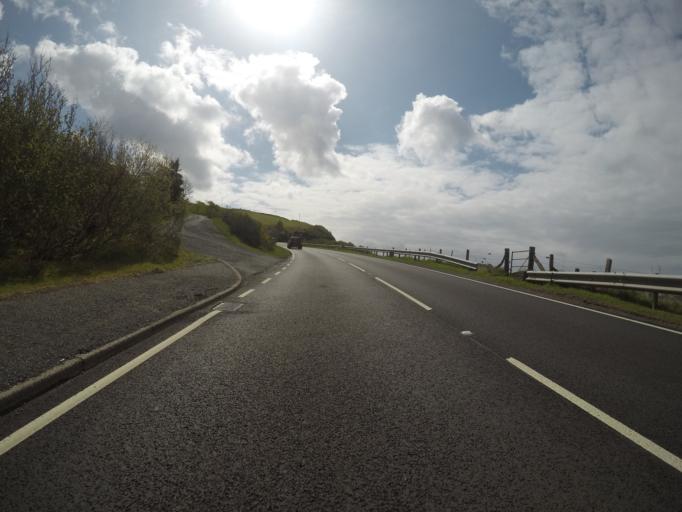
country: GB
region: Scotland
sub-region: Highland
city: Portree
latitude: 57.5821
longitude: -6.3594
